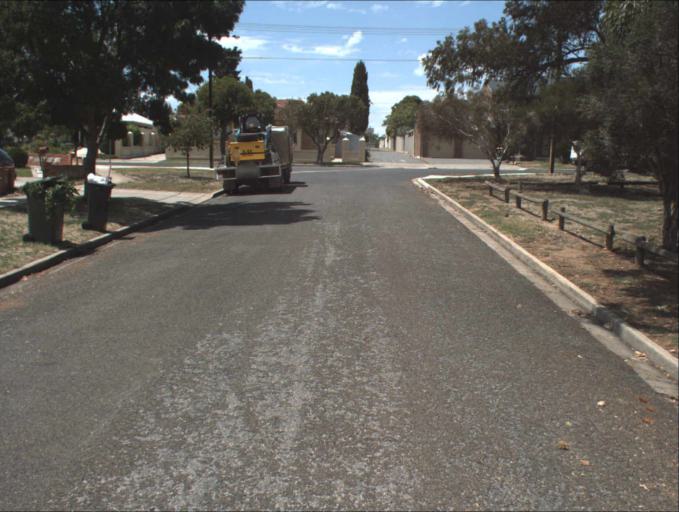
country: AU
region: South Australia
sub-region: Port Adelaide Enfield
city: Enfield
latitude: -34.8514
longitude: 138.6146
